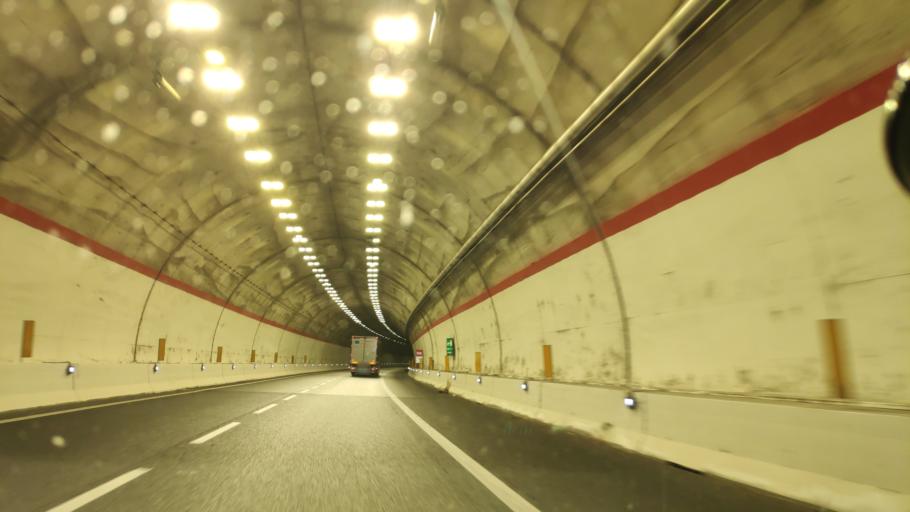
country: IT
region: Campania
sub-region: Provincia di Salerno
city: Sicignano degli Alburni
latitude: 40.5830
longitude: 15.3419
